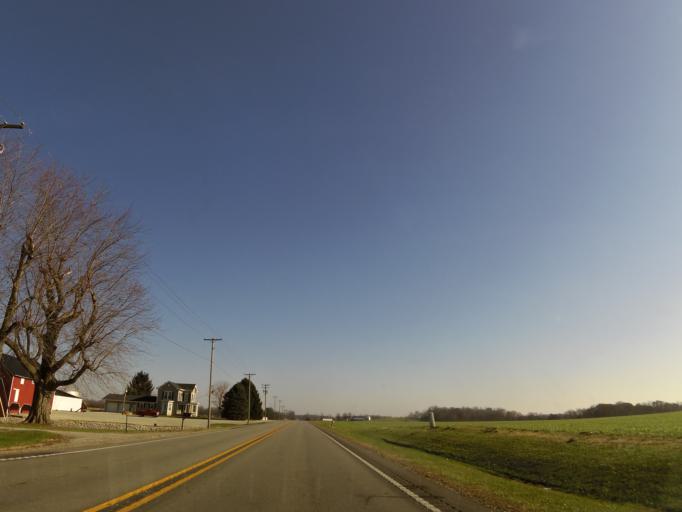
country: US
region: Indiana
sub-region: Fayette County
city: Connersville
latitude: 39.6388
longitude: -85.1005
